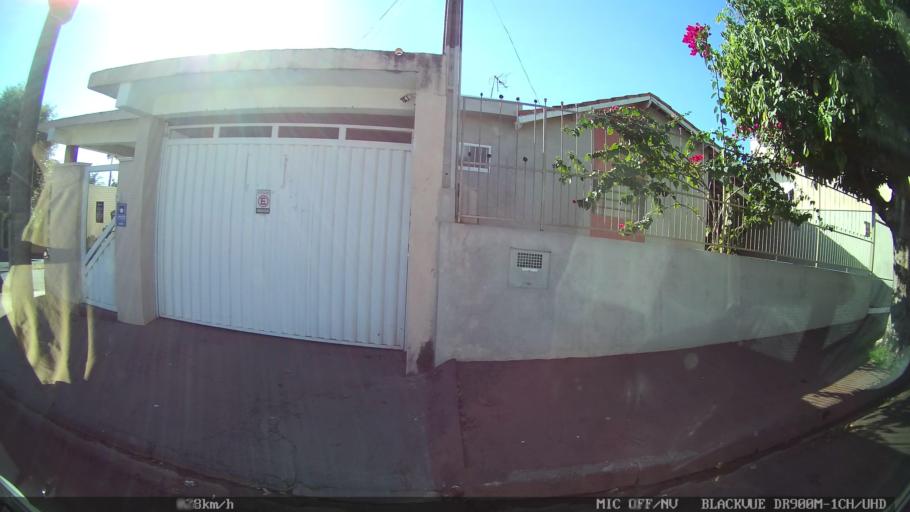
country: BR
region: Sao Paulo
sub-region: Olimpia
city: Olimpia
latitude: -20.7409
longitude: -48.9028
